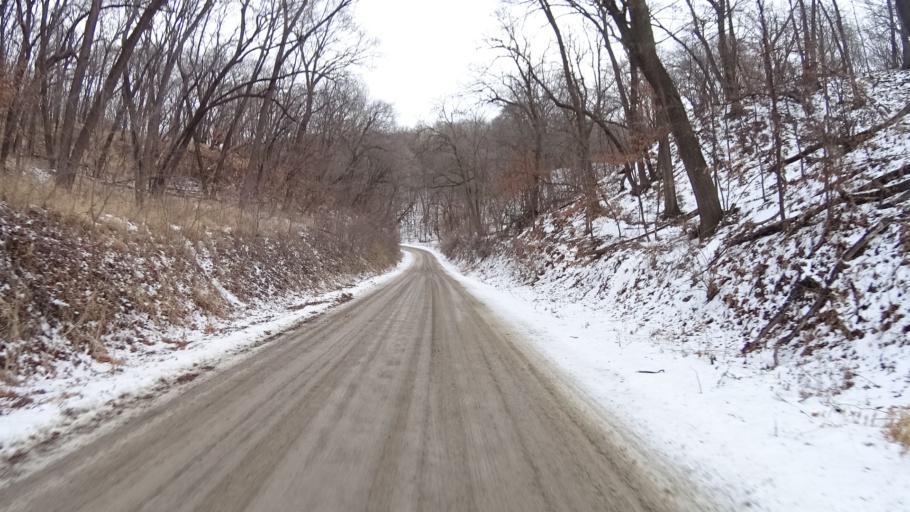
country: US
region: Nebraska
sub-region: Sarpy County
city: Bellevue
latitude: 41.1697
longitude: -95.9011
